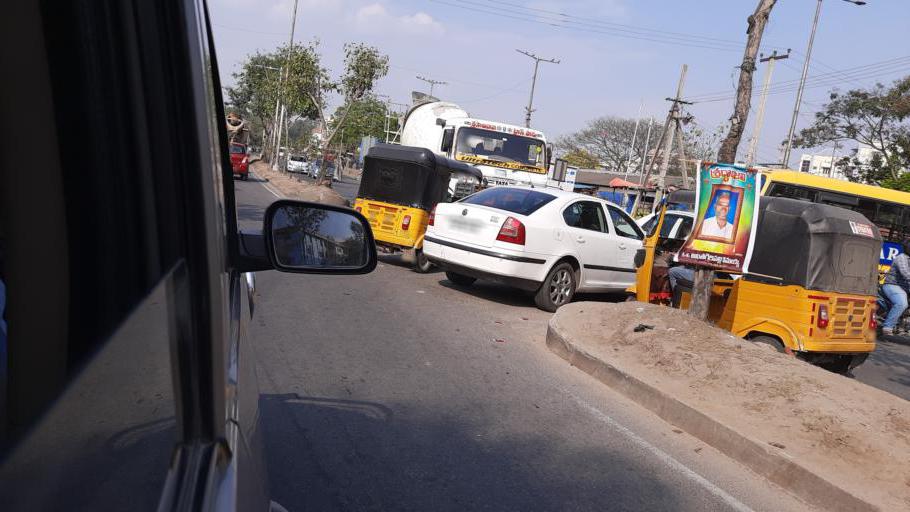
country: IN
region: Telangana
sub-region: Medak
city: Serilingampalle
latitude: 17.4905
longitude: 78.3140
